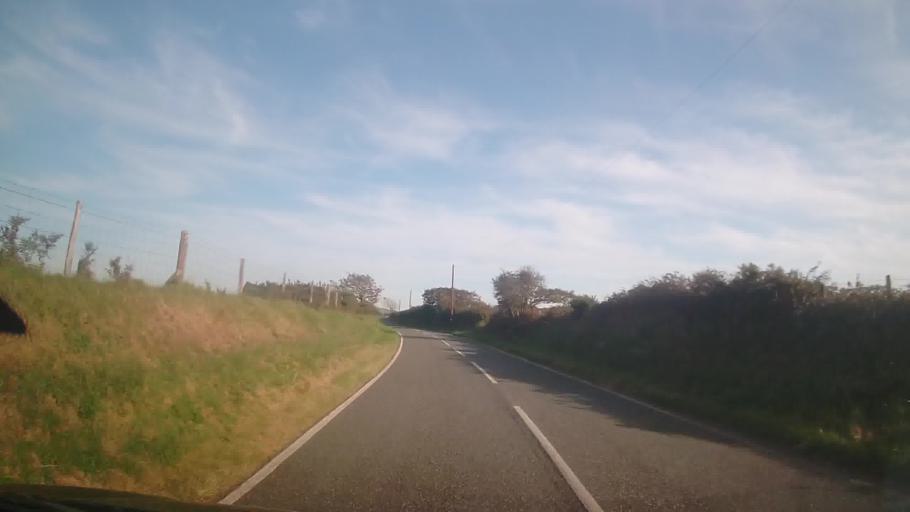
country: GB
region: Wales
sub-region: Pembrokeshire
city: Fishguard
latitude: 51.9716
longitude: -4.9104
